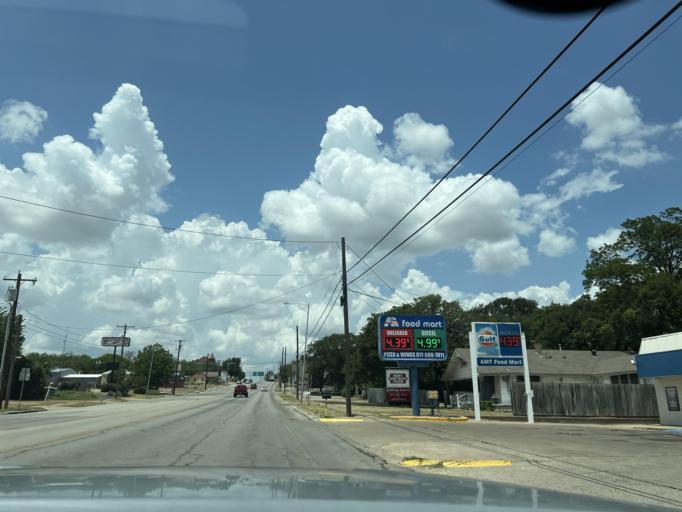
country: US
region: Texas
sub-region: Parker County
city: Weatherford
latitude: 32.7589
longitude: -97.8087
